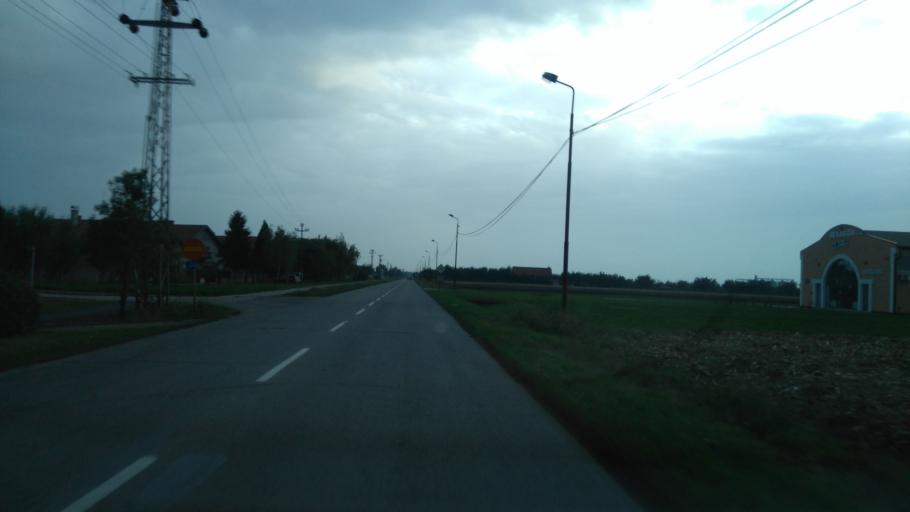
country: RS
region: Autonomna Pokrajina Vojvodina
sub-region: Severnobanatski Okrug
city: Ada
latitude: 45.7848
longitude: 20.1276
